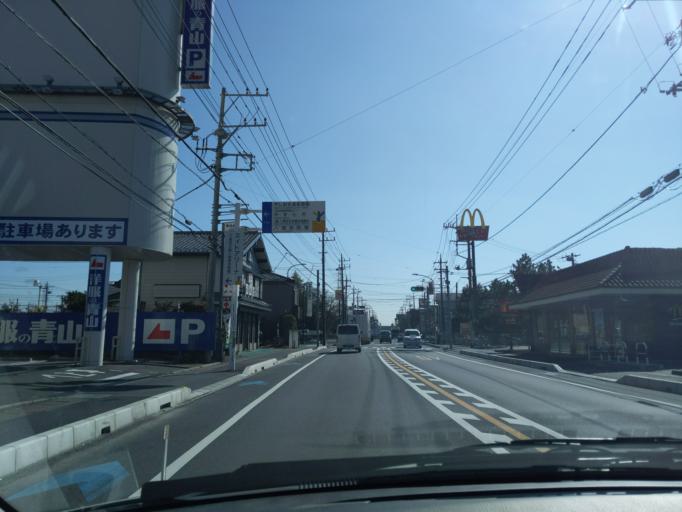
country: JP
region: Saitama
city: Yashio-shi
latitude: 35.8250
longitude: 139.8245
